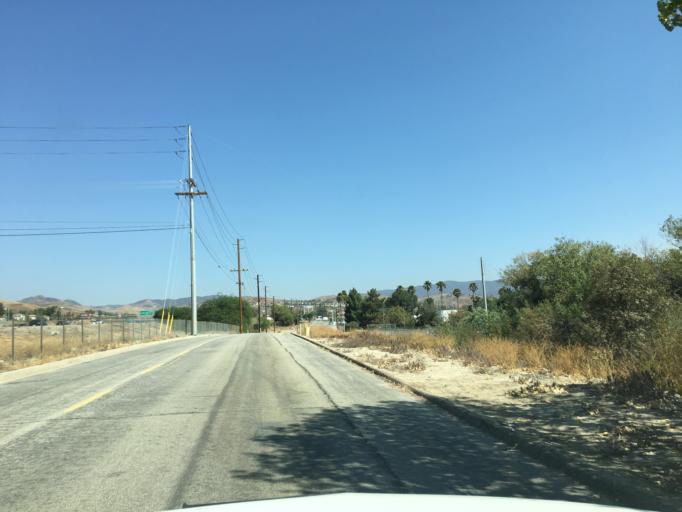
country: US
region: California
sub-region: Los Angeles County
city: Castaic
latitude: 34.4847
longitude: -118.6152
